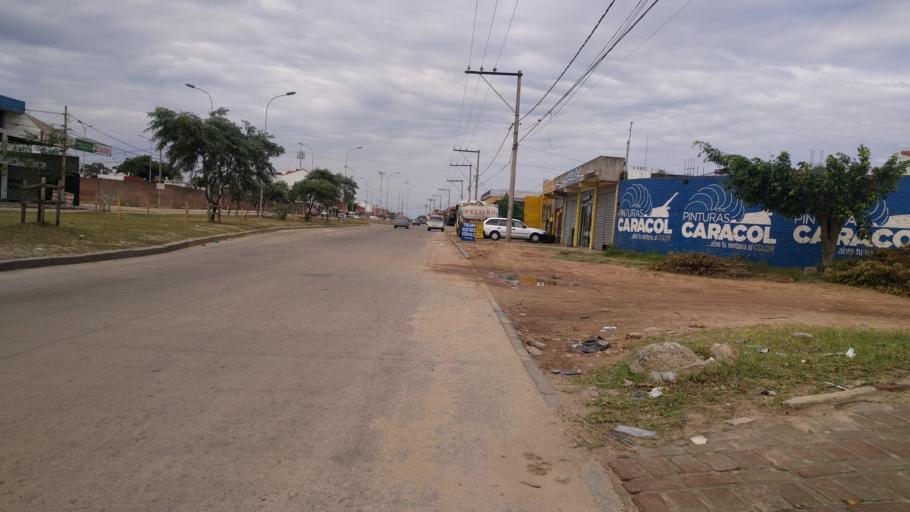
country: BO
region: Santa Cruz
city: Santa Cruz de la Sierra
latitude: -17.8281
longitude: -63.1766
